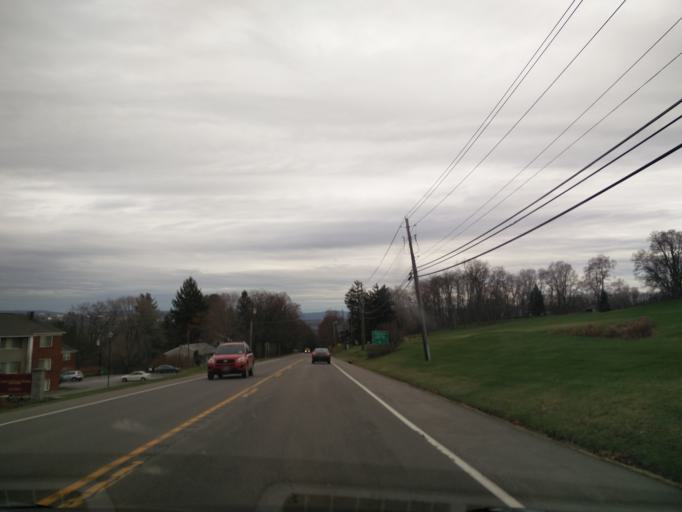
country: US
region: New York
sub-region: Tompkins County
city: Northwest Ithaca
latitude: 42.4600
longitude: -76.5289
